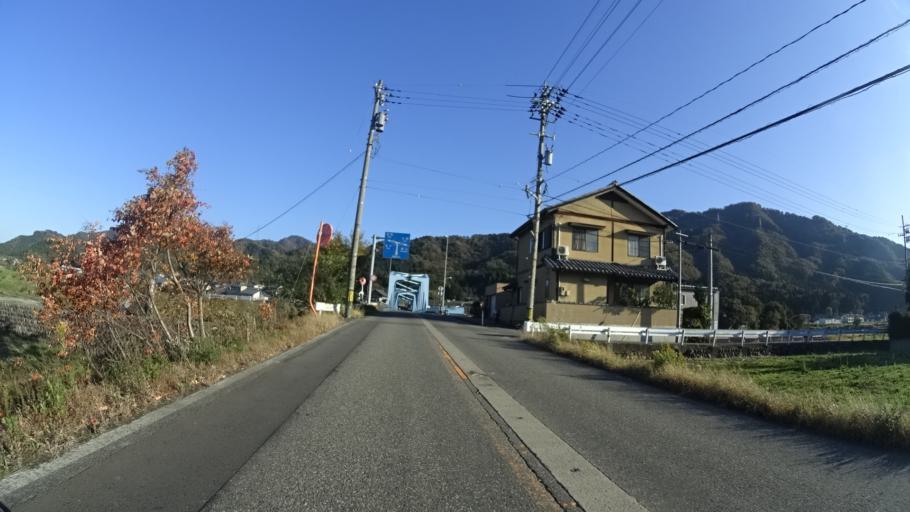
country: JP
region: Fukui
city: Maruoka
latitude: 36.1015
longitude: 136.3271
